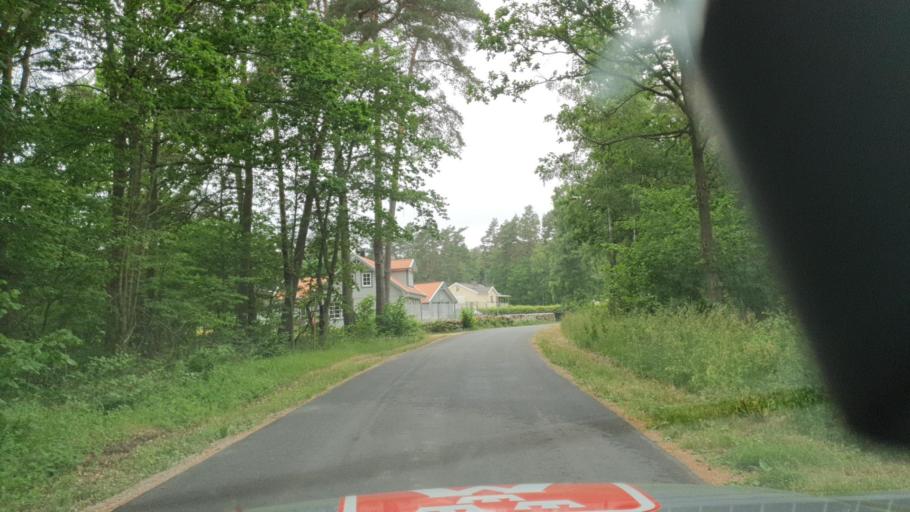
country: SE
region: Kalmar
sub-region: Kalmar Kommun
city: Rinkabyholm
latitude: 56.6509
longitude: 16.2671
